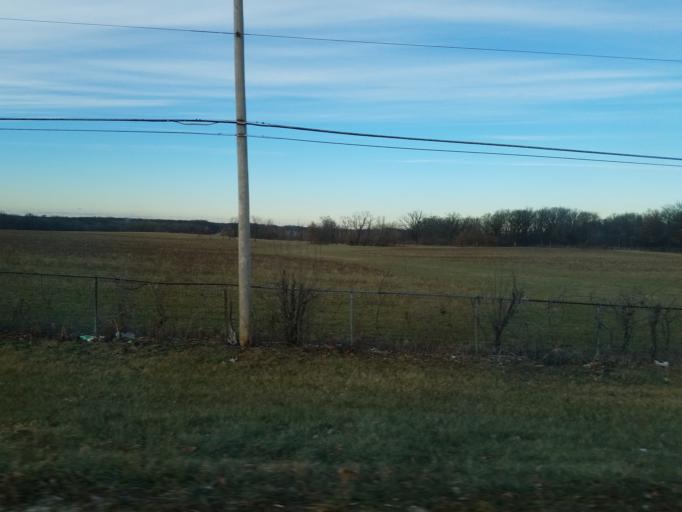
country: US
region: Illinois
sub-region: Will County
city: Goodings Grove
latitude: 41.6285
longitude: -87.9614
